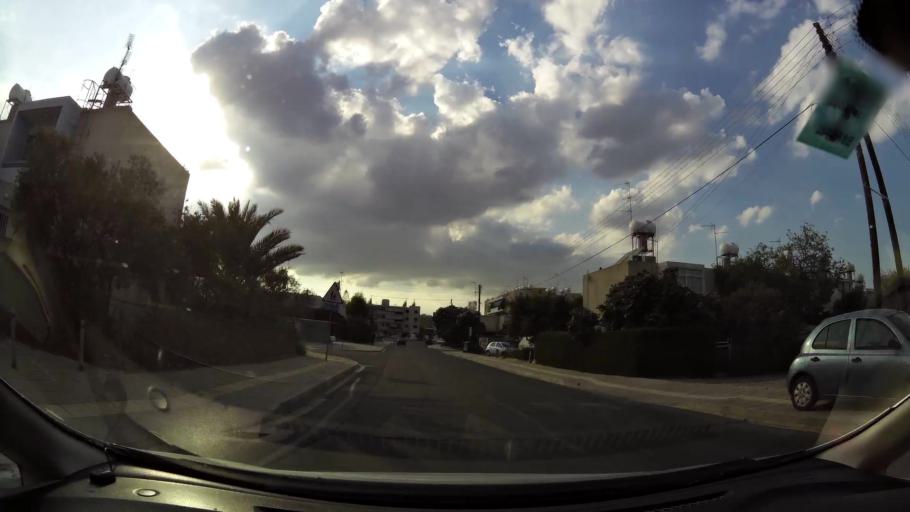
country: CY
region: Lefkosia
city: Kato Deftera
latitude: 35.1058
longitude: 33.2904
